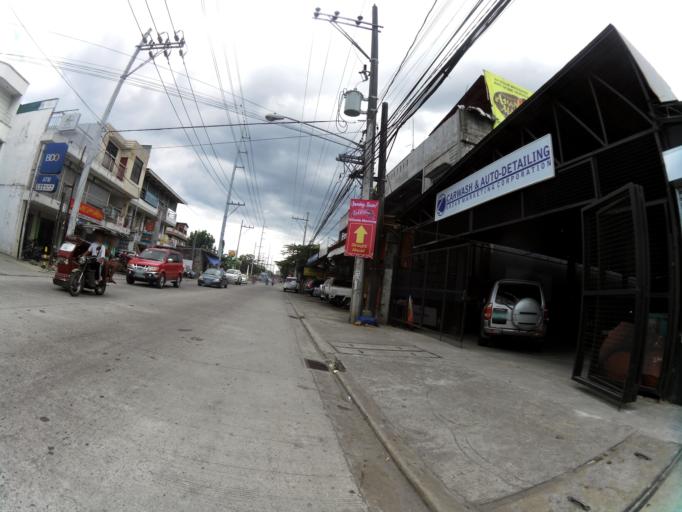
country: PH
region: Calabarzon
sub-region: Province of Rizal
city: Antipolo
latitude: 14.6344
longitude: 121.1215
